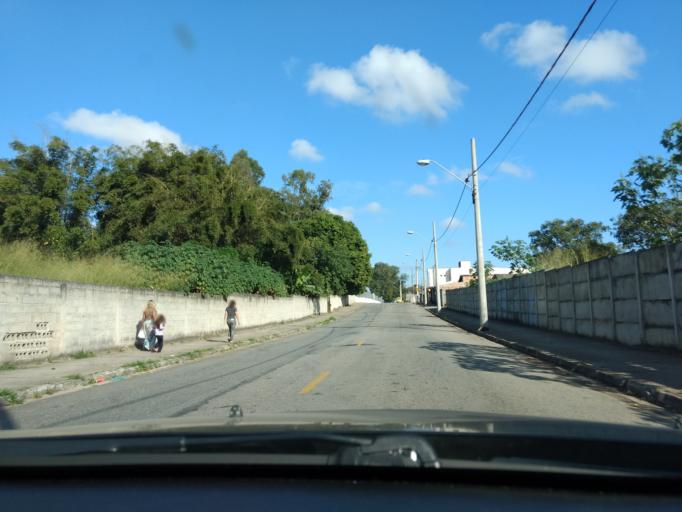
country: BR
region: Sao Paulo
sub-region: Taubate
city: Taubate
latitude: -23.0061
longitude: -45.5221
